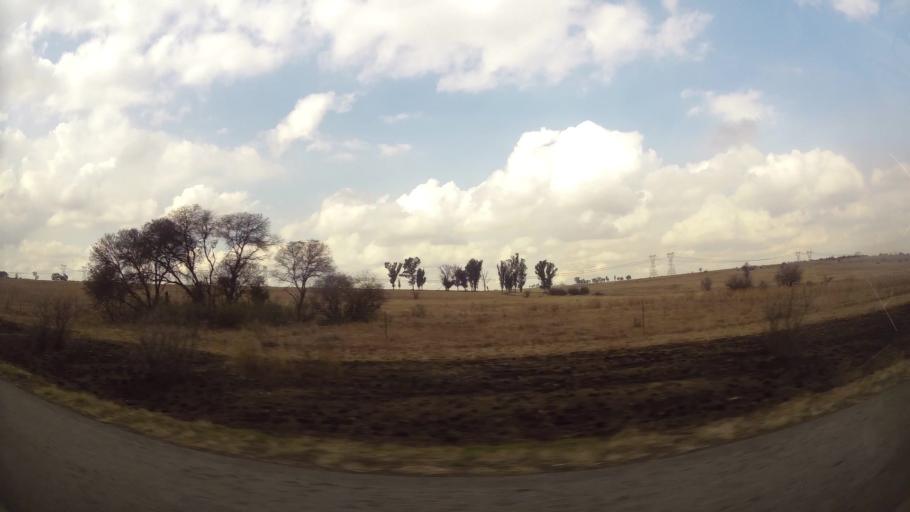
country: ZA
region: Orange Free State
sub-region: Fezile Dabi District Municipality
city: Sasolburg
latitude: -26.7986
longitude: 27.9146
